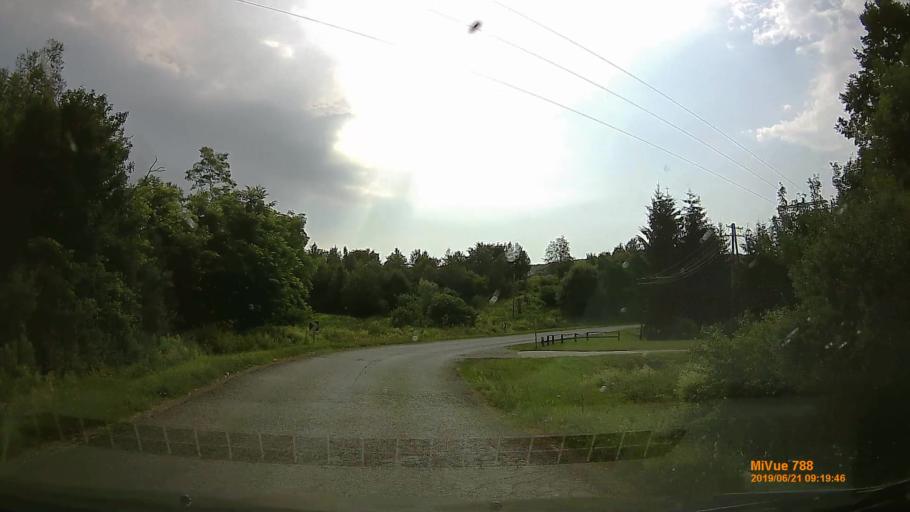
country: HU
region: Somogy
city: Taszar
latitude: 46.2330
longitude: 17.8670
